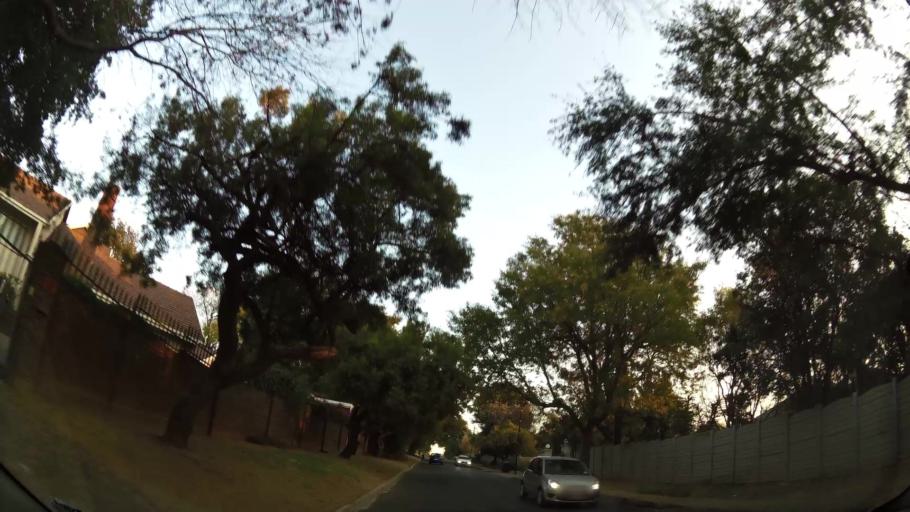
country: ZA
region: Gauteng
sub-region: City of Johannesburg Metropolitan Municipality
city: Johannesburg
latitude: -26.1220
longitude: 27.9947
